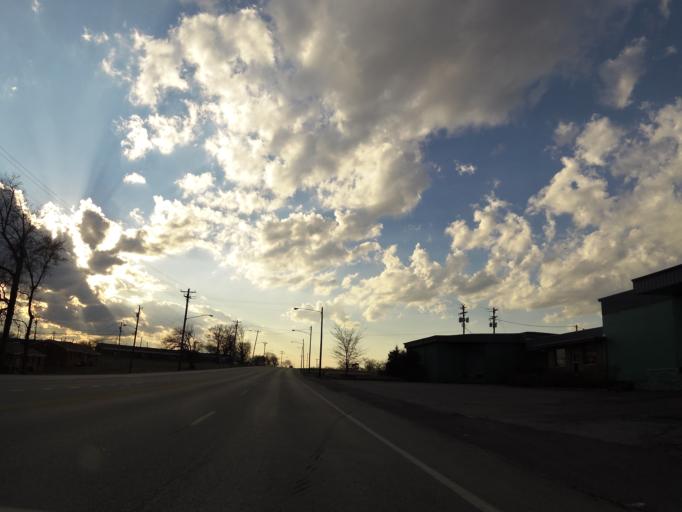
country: US
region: Tennessee
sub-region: Wilson County
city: Lebanon
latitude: 36.2105
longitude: -86.2779
